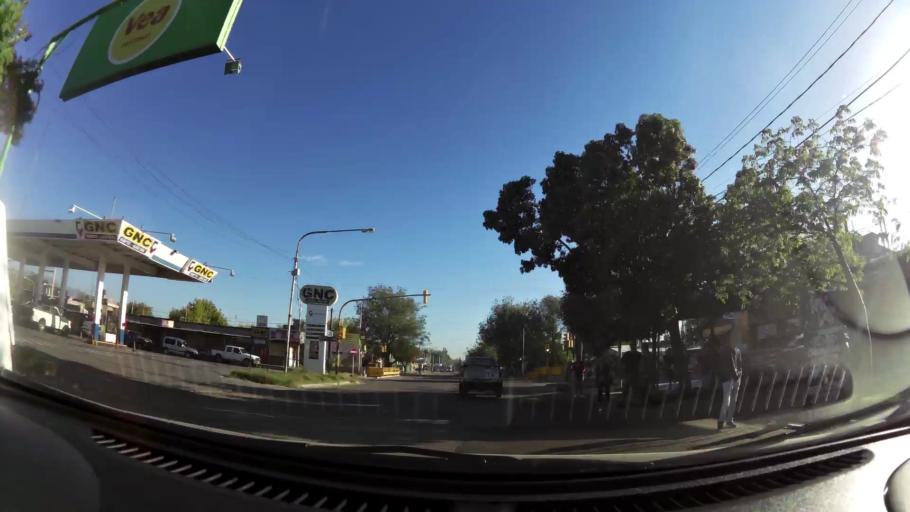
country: AR
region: Mendoza
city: Las Heras
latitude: -32.8628
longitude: -68.8218
